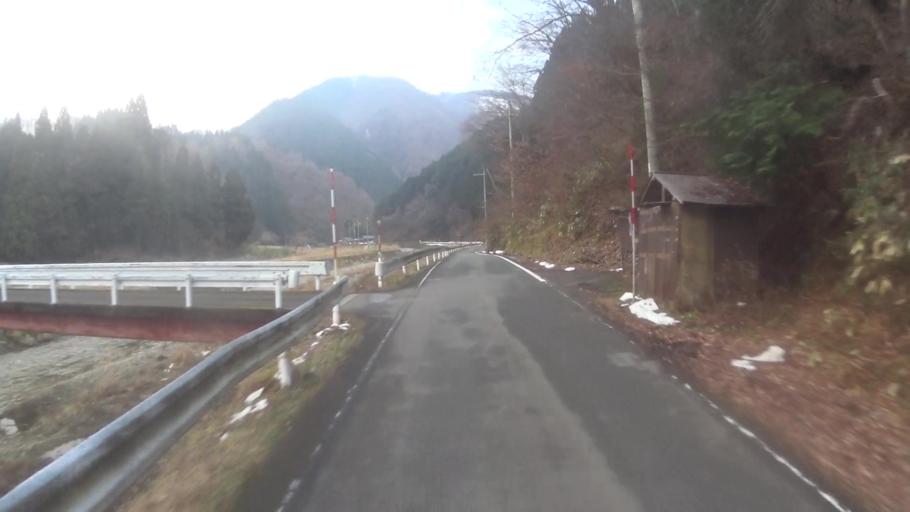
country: JP
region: Kyoto
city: Maizuru
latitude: 35.3908
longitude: 135.4711
